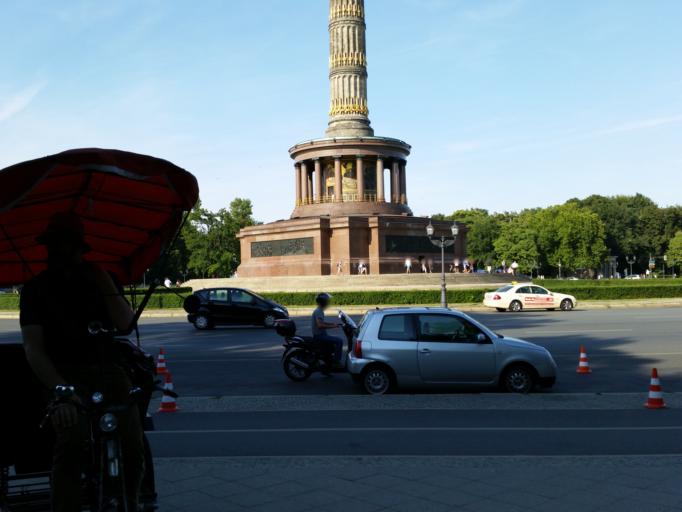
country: DE
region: Berlin
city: Hansaviertel
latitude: 52.5138
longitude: 13.3492
